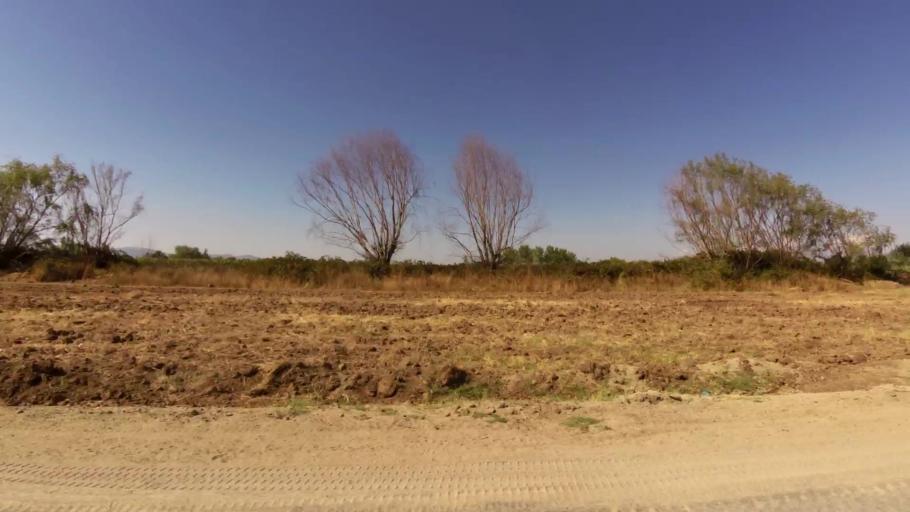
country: CL
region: Maule
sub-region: Provincia de Talca
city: Talca
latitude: -35.4156
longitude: -71.5994
